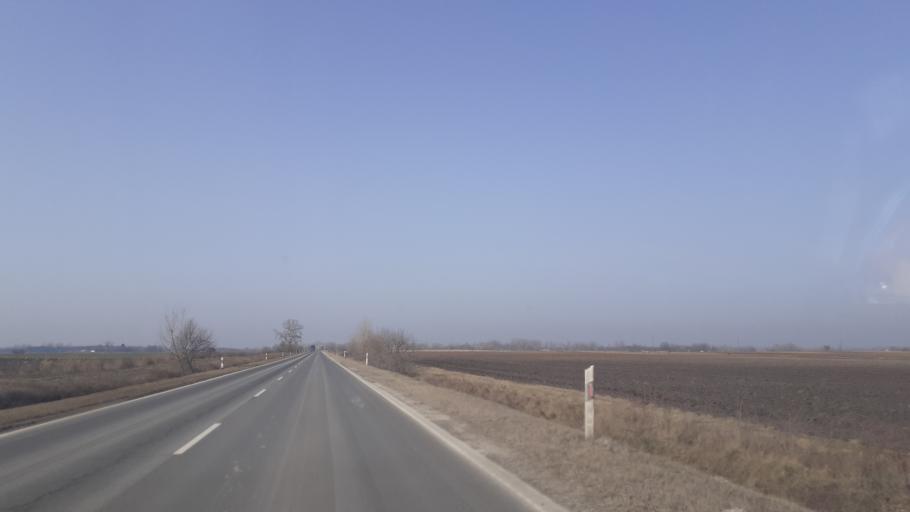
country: HU
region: Pest
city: Bugyi
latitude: 47.2256
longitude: 19.1236
